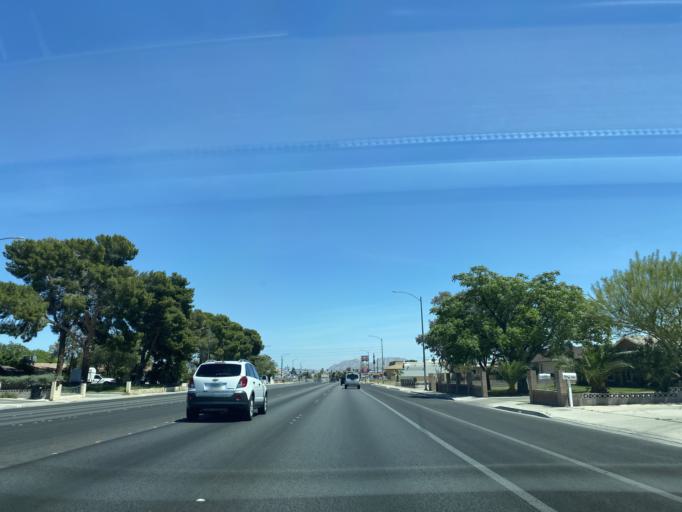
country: US
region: Nevada
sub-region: Clark County
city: Las Vegas
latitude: 36.1955
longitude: -115.2099
